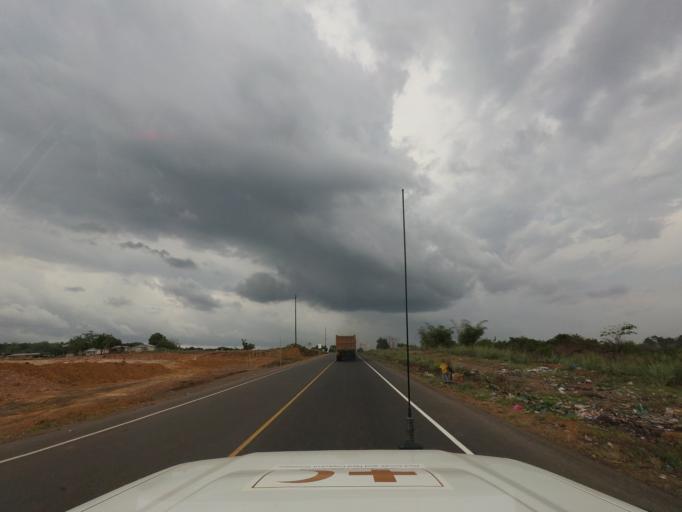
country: LR
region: Margibi
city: Kakata
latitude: 6.5292
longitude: -10.3738
